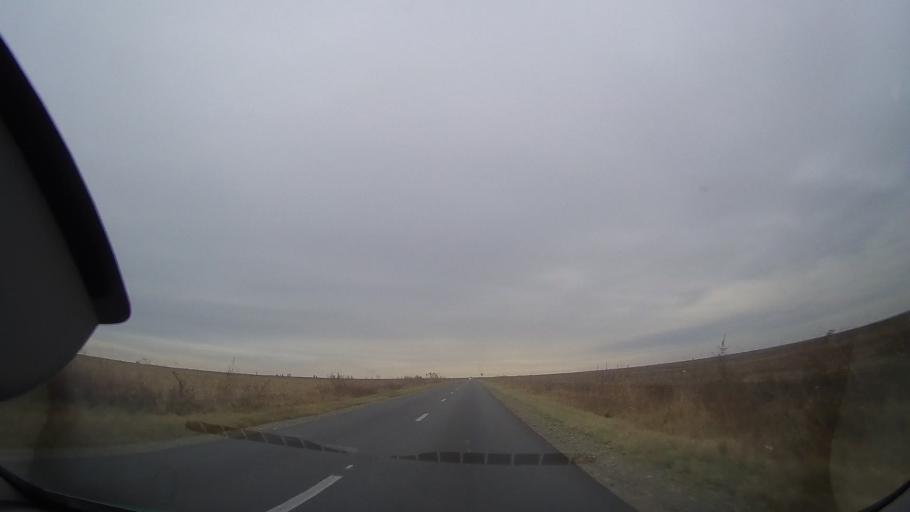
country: RO
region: Ialomita
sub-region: Oras Amara
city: Amara
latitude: 44.6453
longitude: 27.3005
